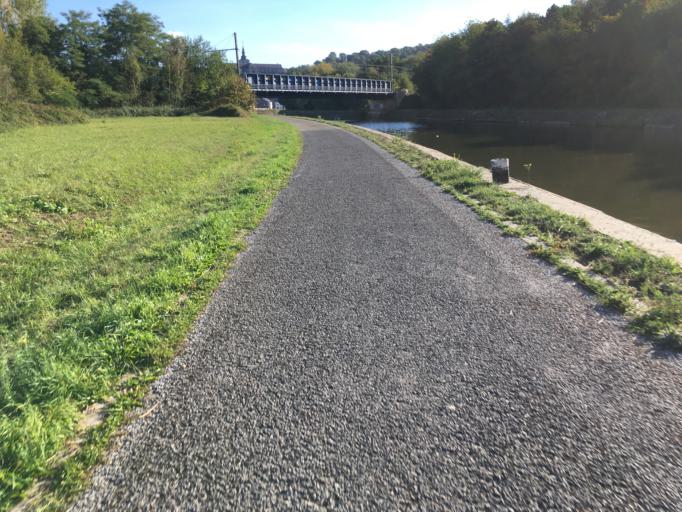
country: BE
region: Wallonia
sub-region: Province de Namur
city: Floreffe
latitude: 50.4413
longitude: 4.7577
